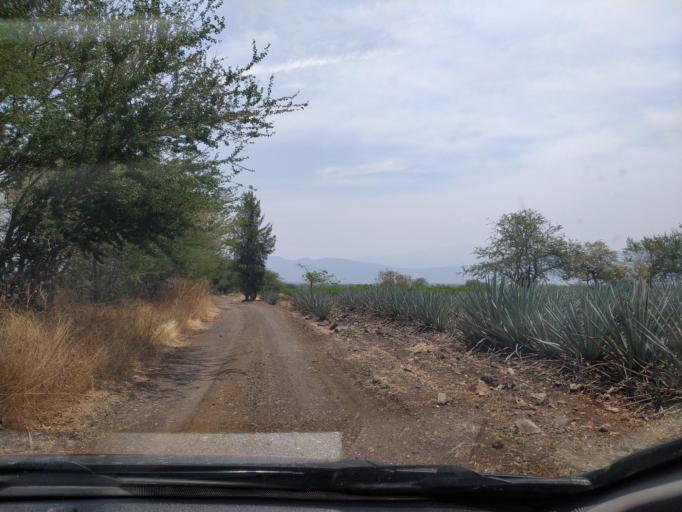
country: MX
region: Jalisco
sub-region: Zacoalco de Torres
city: Barranca de Otates (Barranca de Otatan)
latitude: 20.2745
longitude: -103.6295
